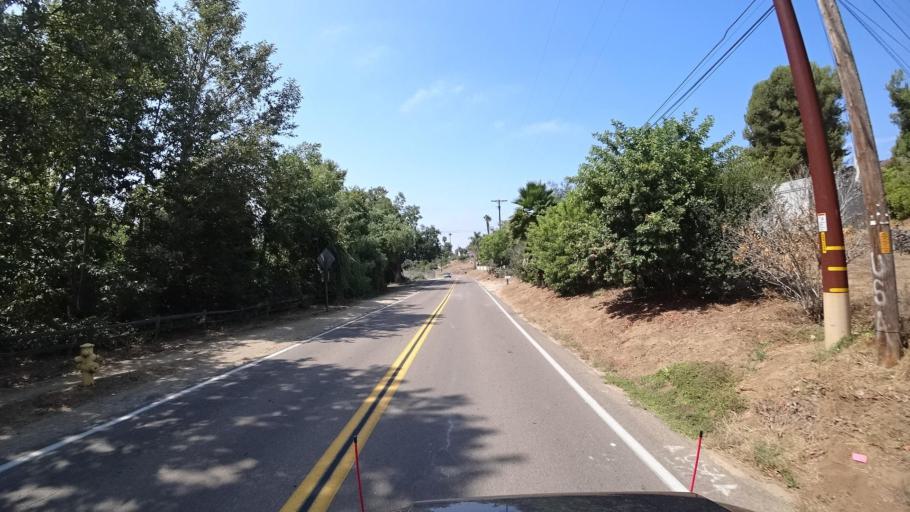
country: US
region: California
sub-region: San Diego County
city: Fallbrook
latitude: 33.3542
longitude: -117.2343
